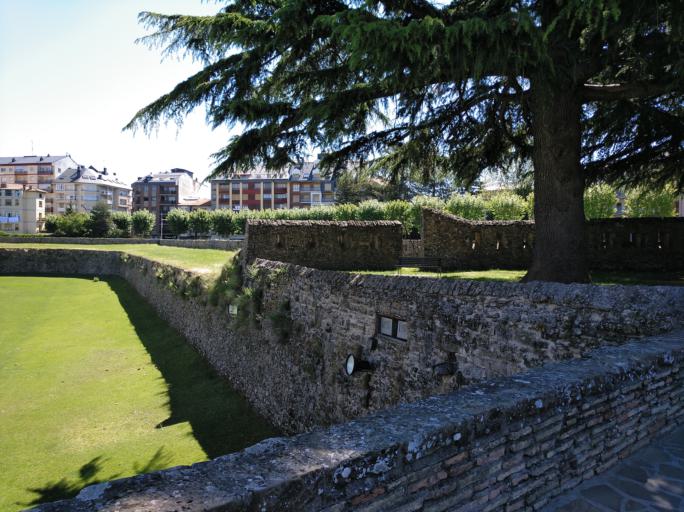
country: ES
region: Aragon
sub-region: Provincia de Huesca
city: Jaca
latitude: 42.5717
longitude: -0.5514
